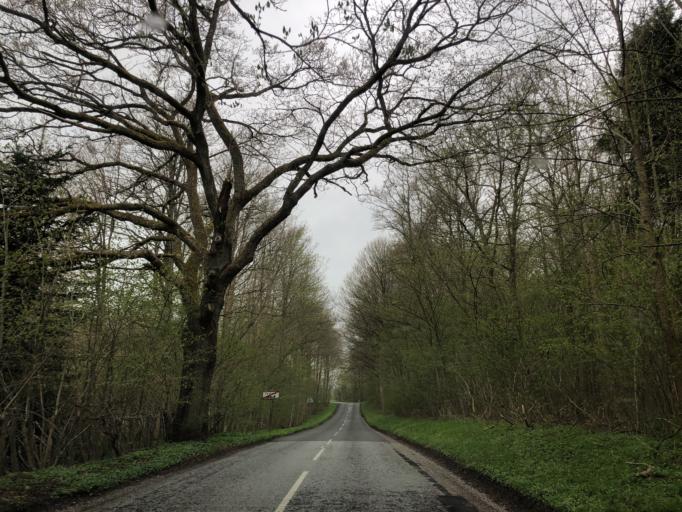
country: DK
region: Zealand
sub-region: Lejre Kommune
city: Kirke Hvalso
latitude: 55.5261
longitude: 11.8606
